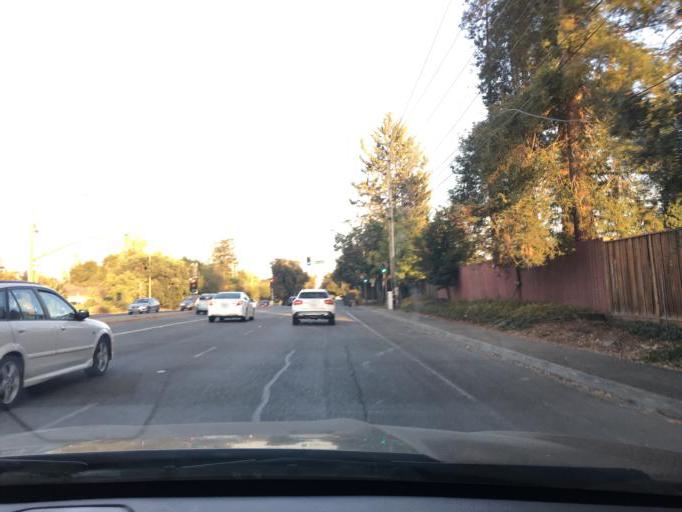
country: US
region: California
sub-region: Santa Clara County
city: Saratoga
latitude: 37.2933
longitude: -122.0087
